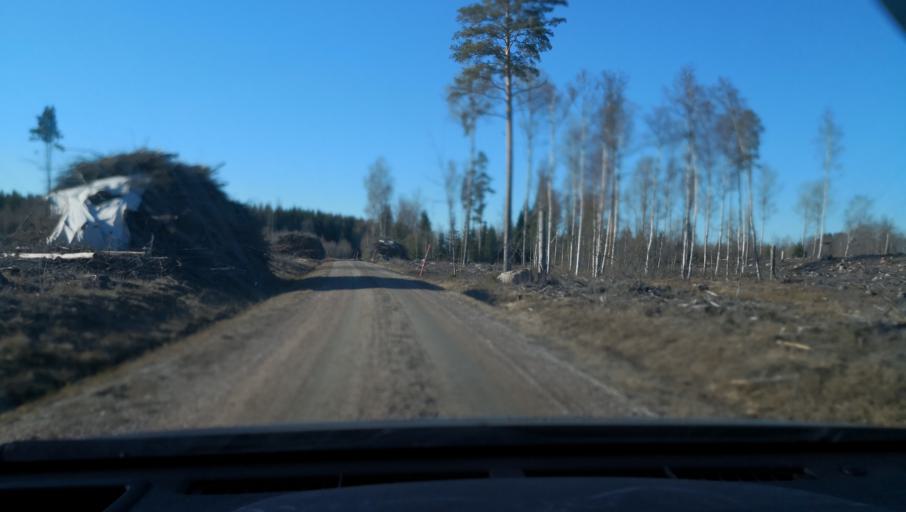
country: SE
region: Dalarna
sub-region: Avesta Kommun
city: Horndal
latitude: 60.1768
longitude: 16.6309
